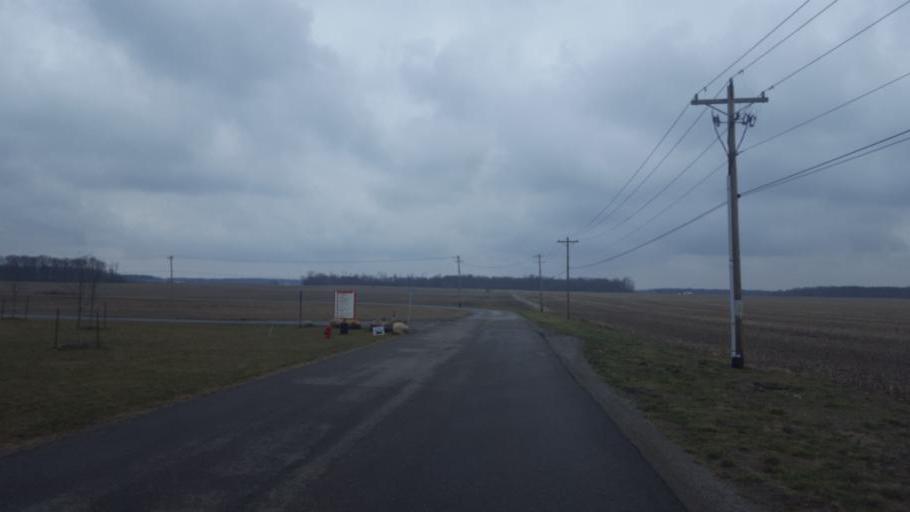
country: US
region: Ohio
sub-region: Delaware County
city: Ashley
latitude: 40.3787
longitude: -82.8295
